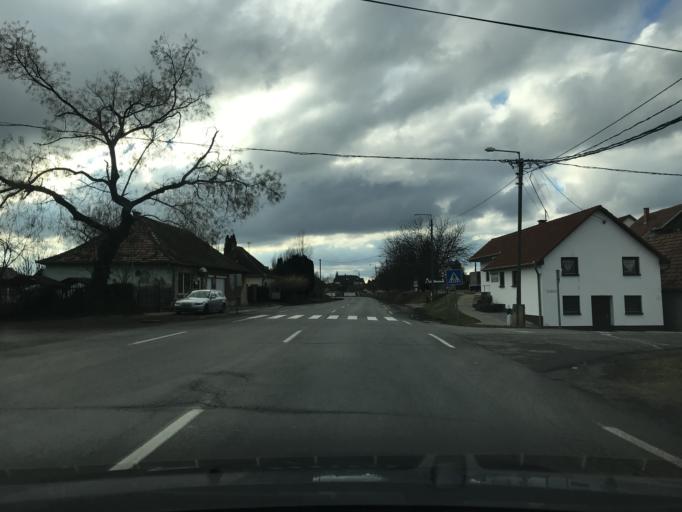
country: HU
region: Bacs-Kiskun
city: Nemesnadudvar
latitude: 46.3332
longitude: 19.0593
